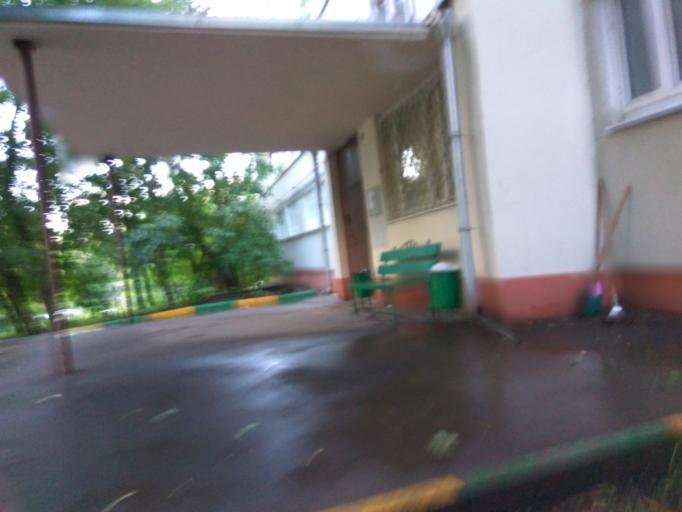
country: RU
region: Moskovskaya
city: Bol'shaya Setun'
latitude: 55.7145
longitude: 37.3984
